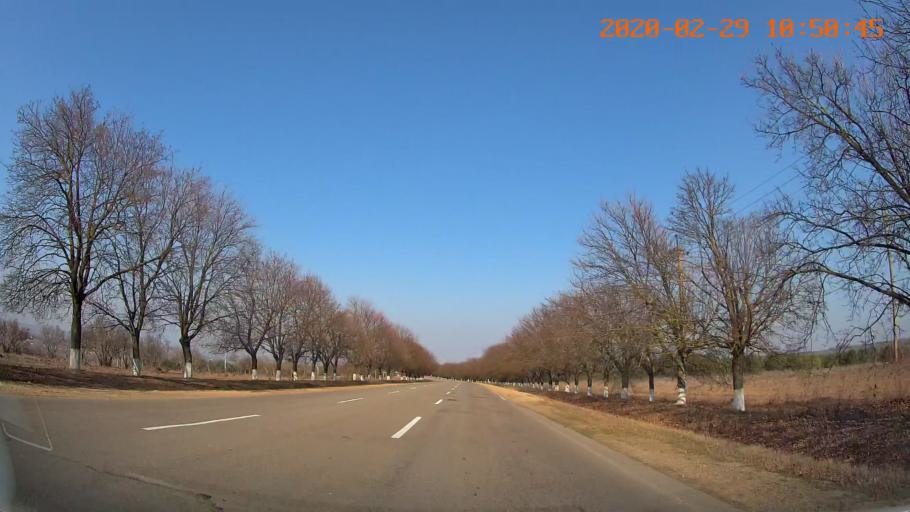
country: MD
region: Telenesti
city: Grigoriopol
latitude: 47.0862
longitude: 29.3724
